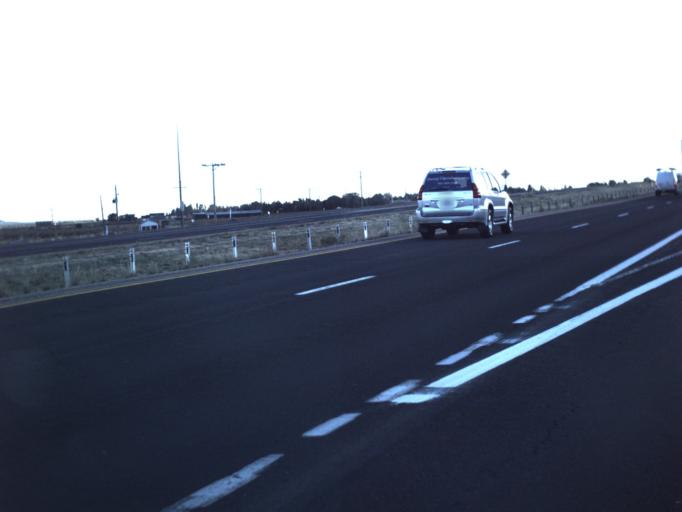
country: US
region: Utah
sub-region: Iron County
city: Cedar City
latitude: 37.5995
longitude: -113.1635
